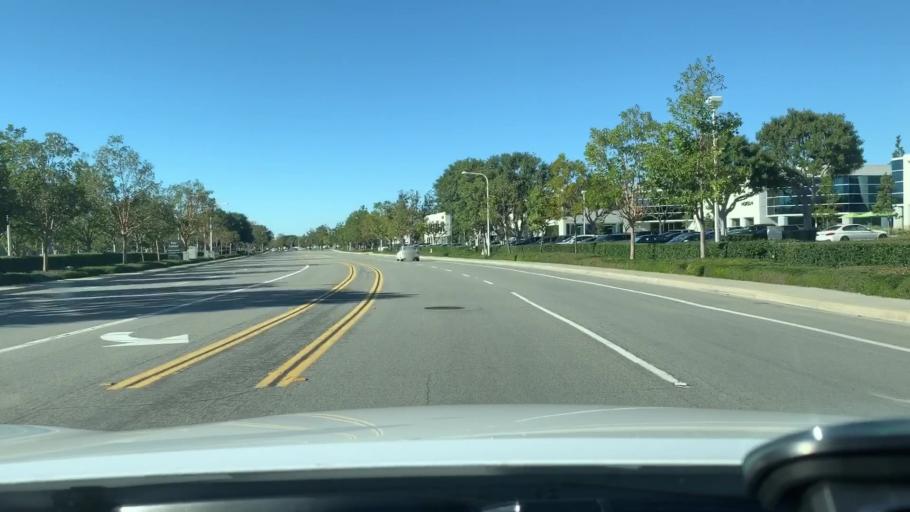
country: US
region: California
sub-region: Orange County
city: Laguna Woods
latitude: 33.6637
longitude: -117.7445
